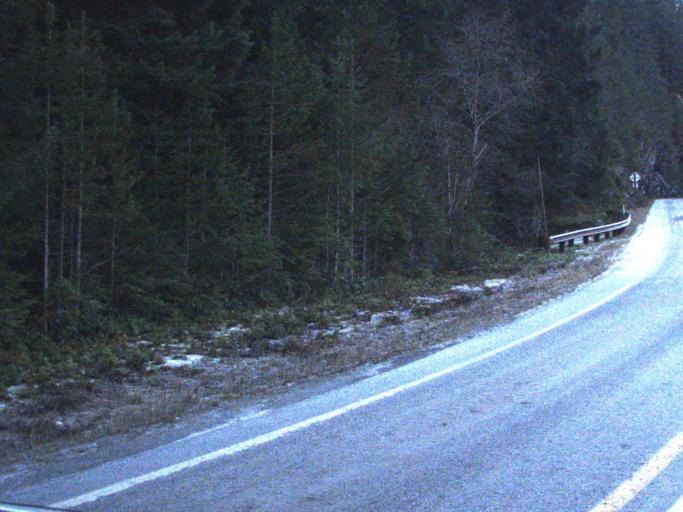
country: US
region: Washington
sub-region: Snohomish County
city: Darrington
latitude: 48.7109
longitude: -121.1225
